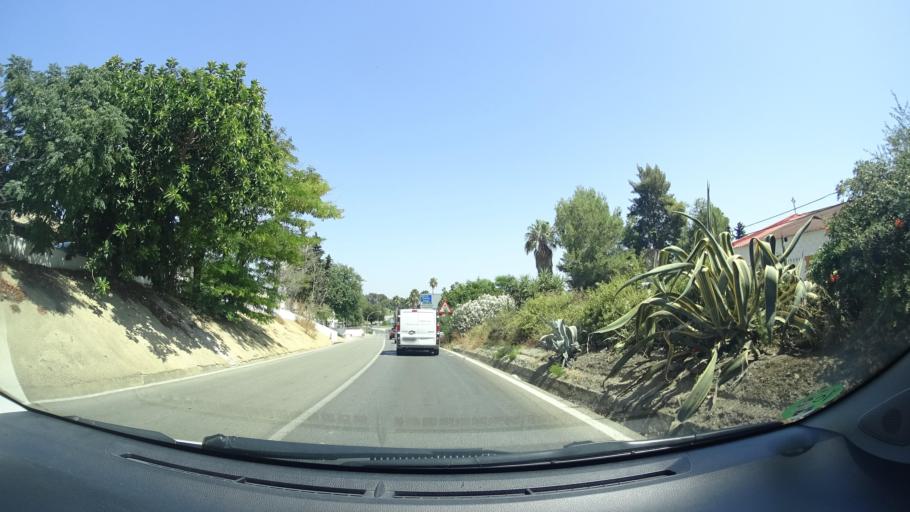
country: ES
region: Andalusia
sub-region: Provincia de Cadiz
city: Jerez de la Frontera
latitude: 36.6592
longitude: -6.1023
